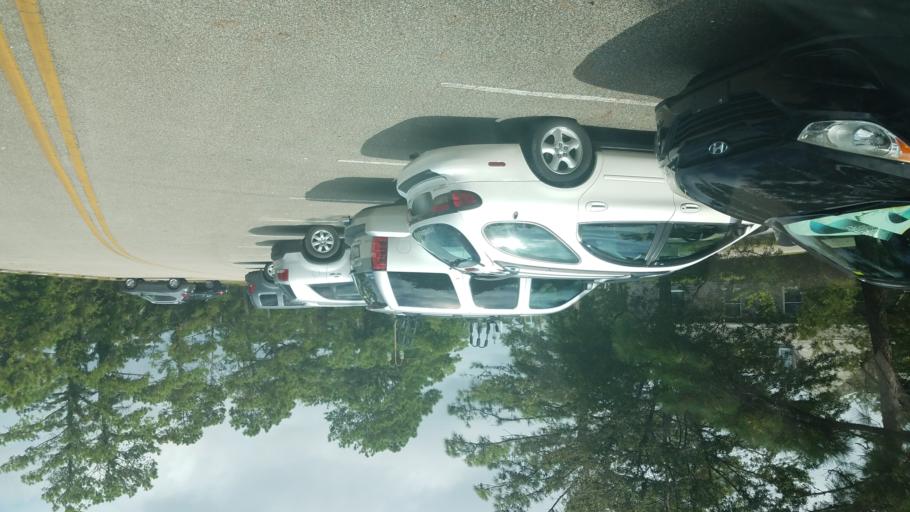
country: US
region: North Carolina
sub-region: Dare County
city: Manteo
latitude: 35.9118
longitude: -75.6663
